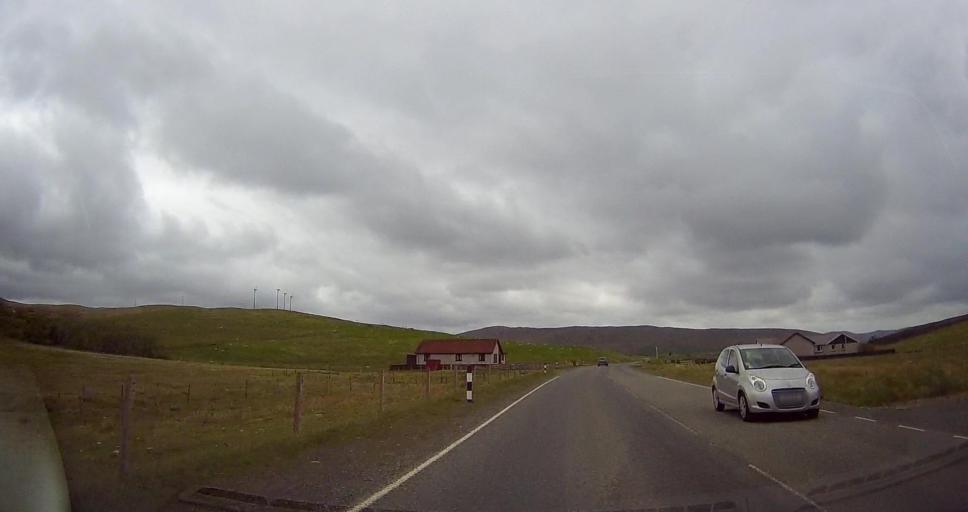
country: GB
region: Scotland
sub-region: Shetland Islands
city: Lerwick
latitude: 60.3793
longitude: -1.3415
